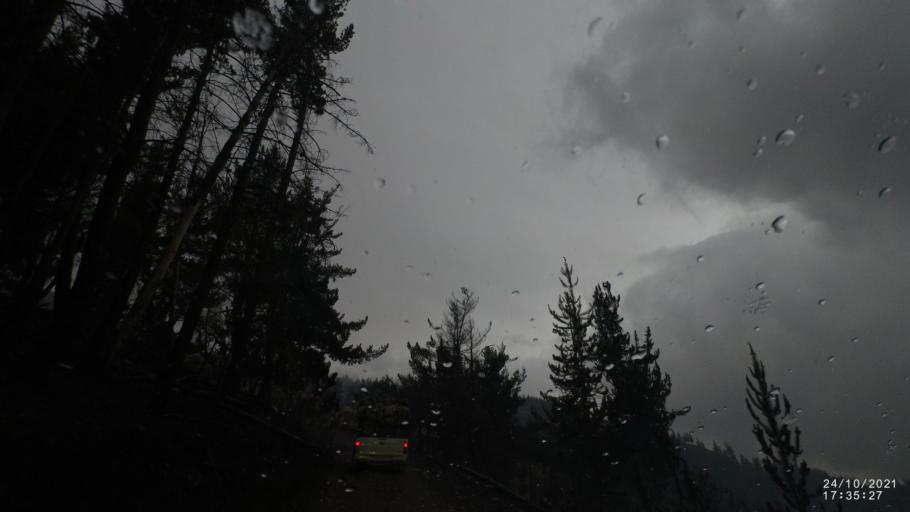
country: BO
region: Cochabamba
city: Cochabamba
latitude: -17.3204
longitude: -66.1283
